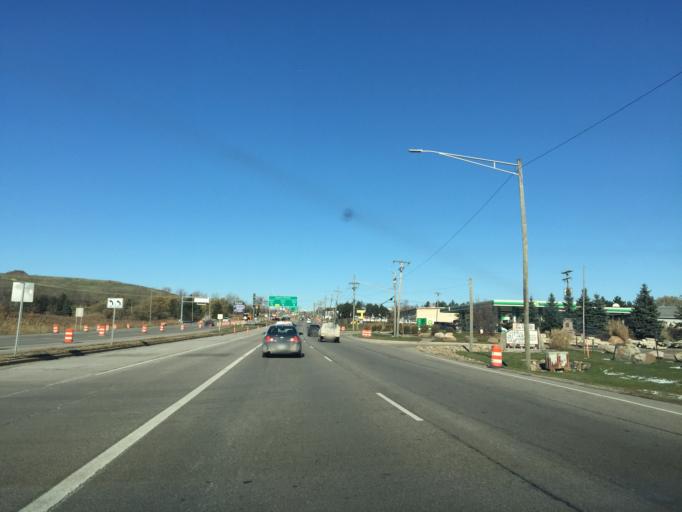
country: US
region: Michigan
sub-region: Oakland County
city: Auburn Hills
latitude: 42.6944
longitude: -83.2420
